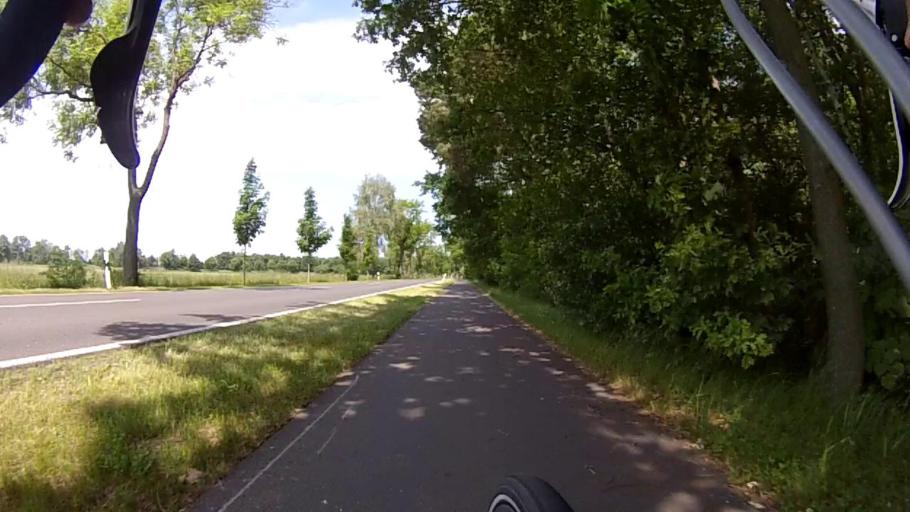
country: DE
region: Brandenburg
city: Liebenwalde
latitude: 52.8554
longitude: 13.4016
